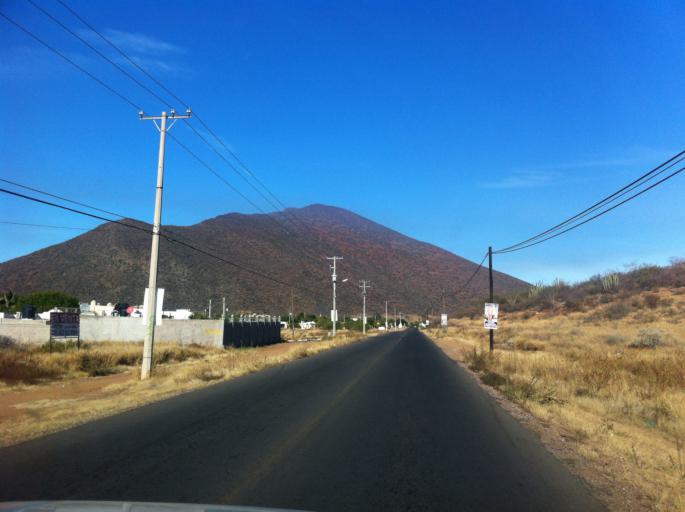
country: MX
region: Sonora
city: Heroica Guaymas
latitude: 27.9274
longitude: -110.9343
